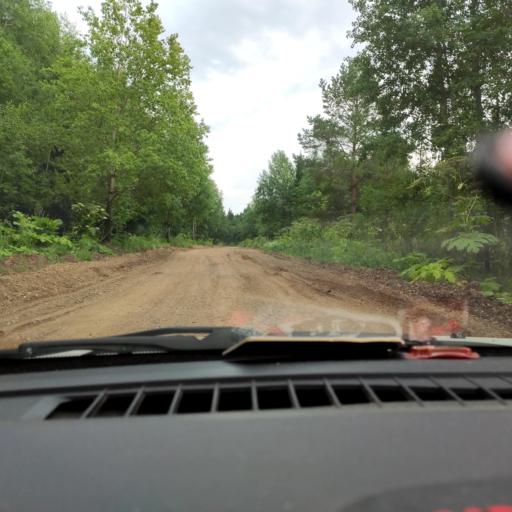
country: RU
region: Perm
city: Kultayevo
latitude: 57.8167
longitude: 56.0006
